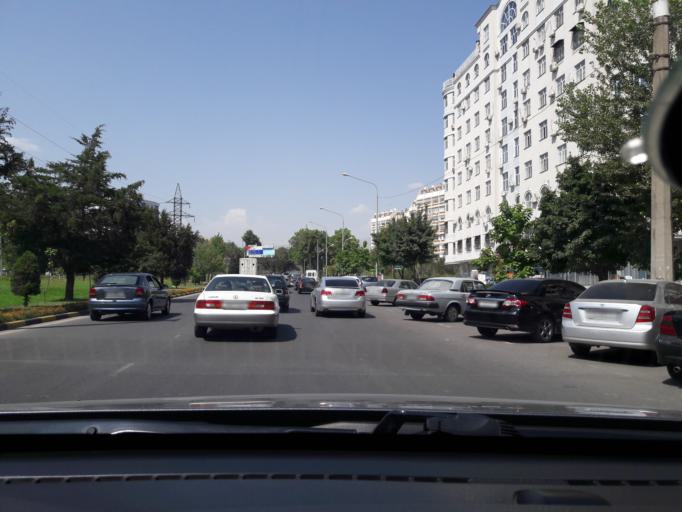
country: TJ
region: Dushanbe
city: Dushanbe
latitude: 38.5902
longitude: 68.7422
